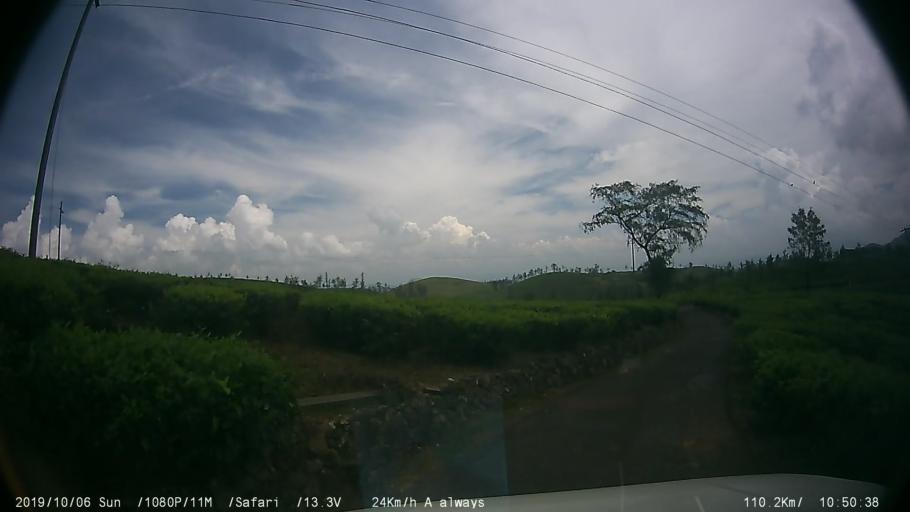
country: IN
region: Kerala
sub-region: Kottayam
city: Erattupetta
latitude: 9.6193
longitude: 76.9546
